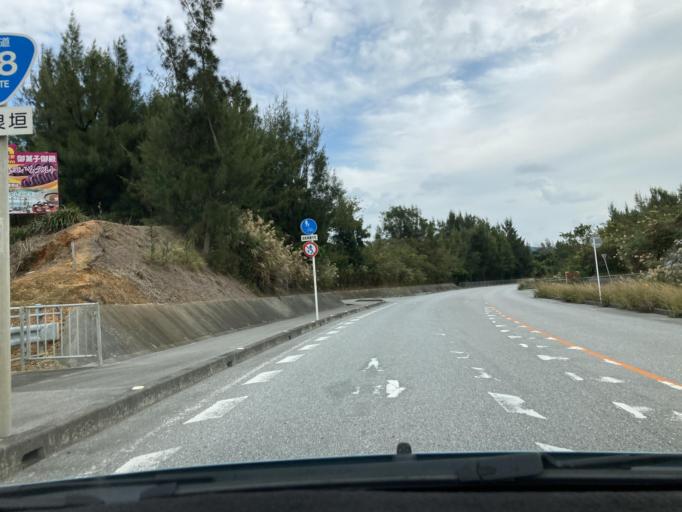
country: JP
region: Okinawa
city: Ishikawa
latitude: 26.5047
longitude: 127.8714
